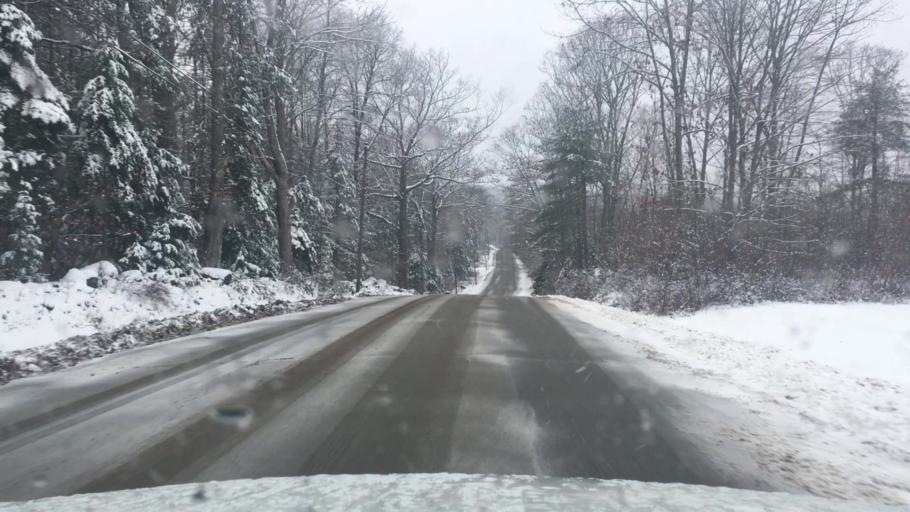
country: US
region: Maine
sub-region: Lincoln County
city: Jefferson
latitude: 44.1844
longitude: -69.3858
